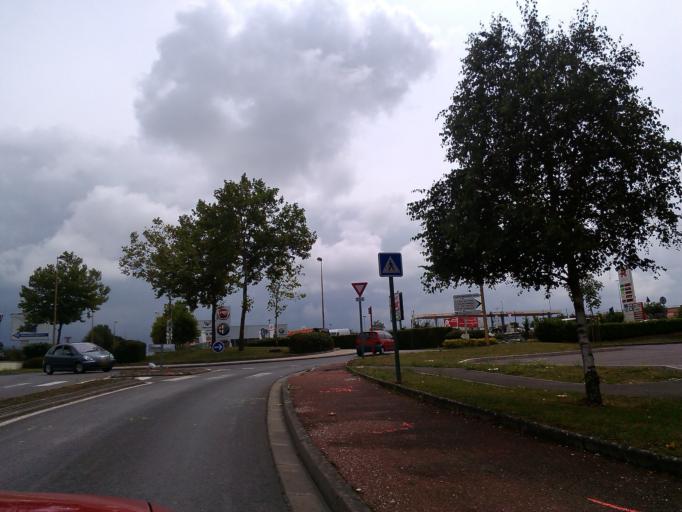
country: FR
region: Poitou-Charentes
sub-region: Departement de la Charente
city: Saint-Brice
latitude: 45.6857
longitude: -0.3055
